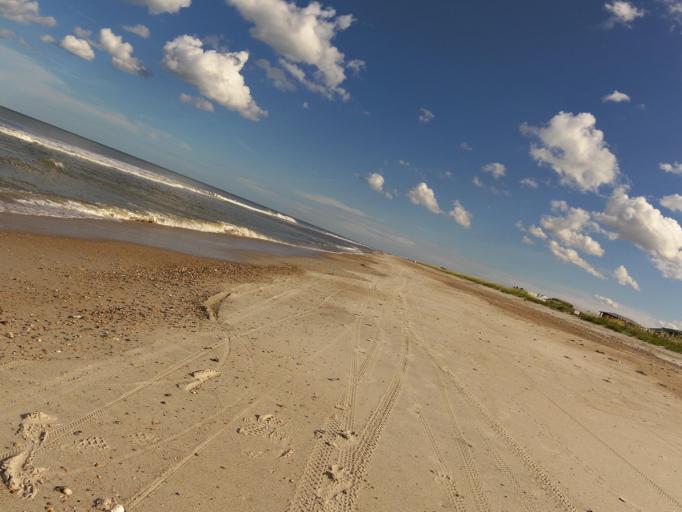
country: US
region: Florida
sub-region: Nassau County
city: Fernandina Beach
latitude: 30.6918
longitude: -81.4278
